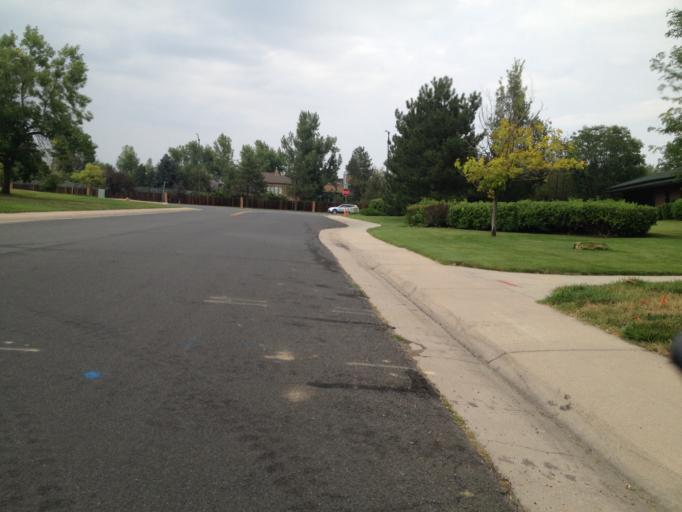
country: US
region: Colorado
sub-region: Boulder County
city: Louisville
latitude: 39.9861
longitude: -105.1600
